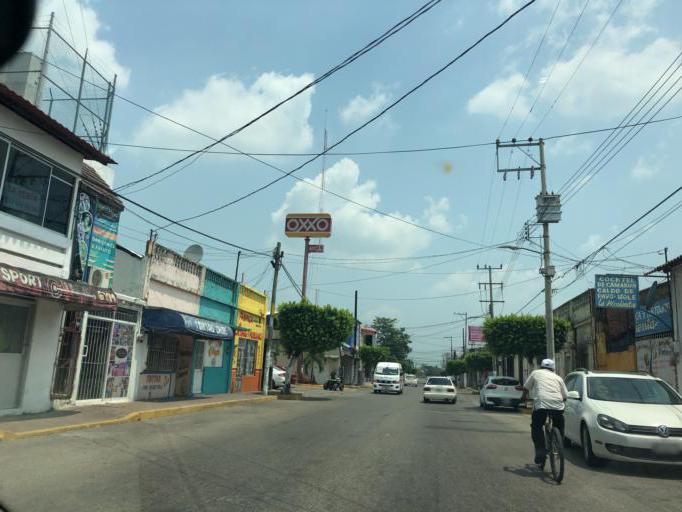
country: MX
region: Tabasco
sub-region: Cardenas
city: Cardenas
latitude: 17.9843
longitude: -93.3768
